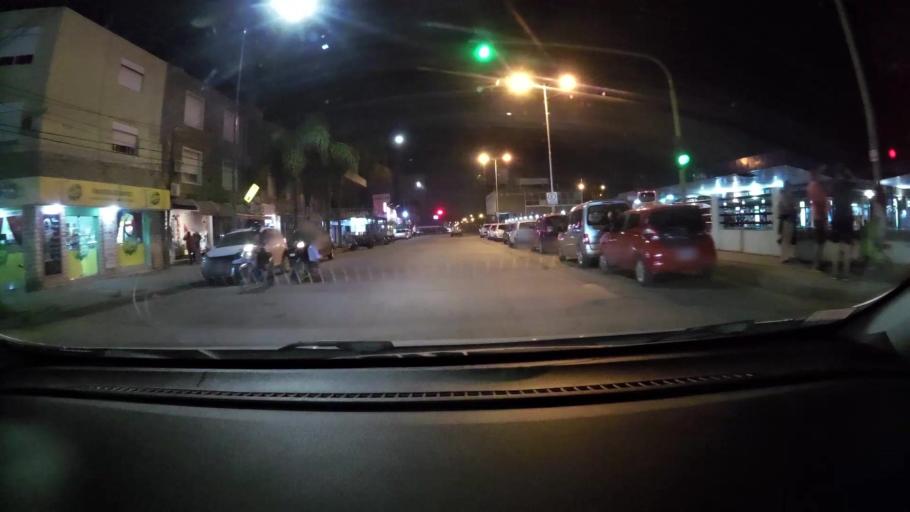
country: AR
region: Cordoba
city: Villa Maria
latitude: -32.4144
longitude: -63.2319
